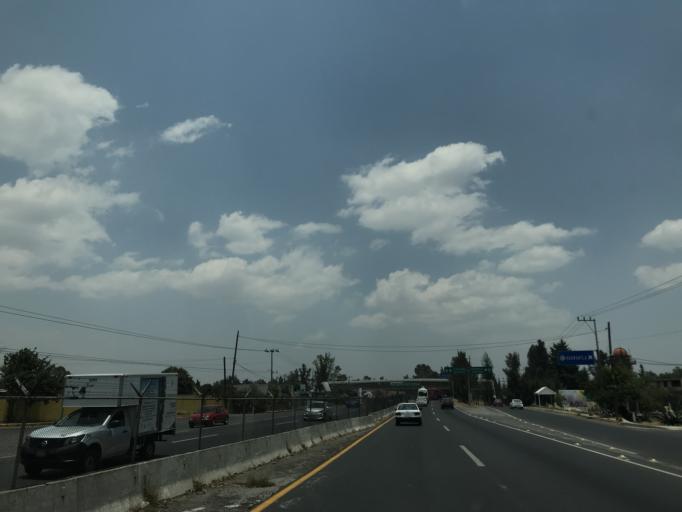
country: MX
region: Tlaxcala
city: Yauhquemehcan
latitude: 19.3893
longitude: -98.1770
